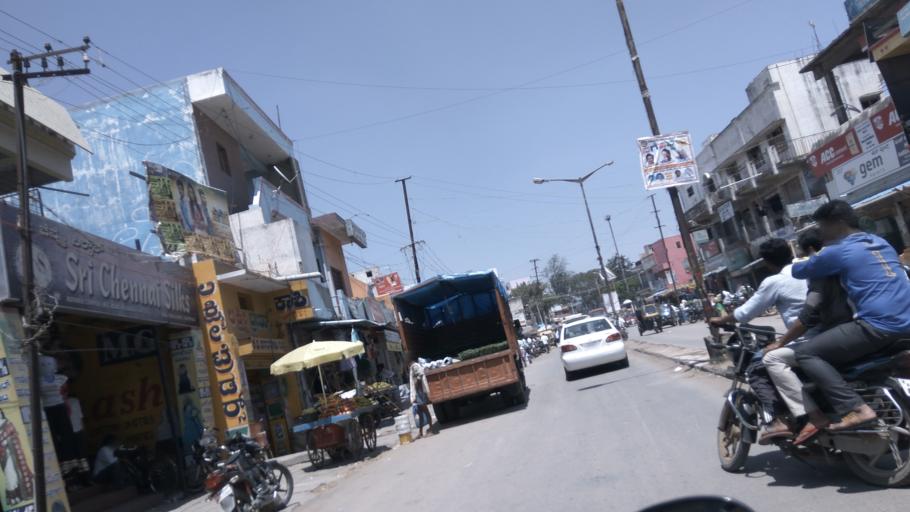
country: IN
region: Karnataka
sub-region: Kolar
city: Mulbagal
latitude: 13.1632
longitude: 78.3936
